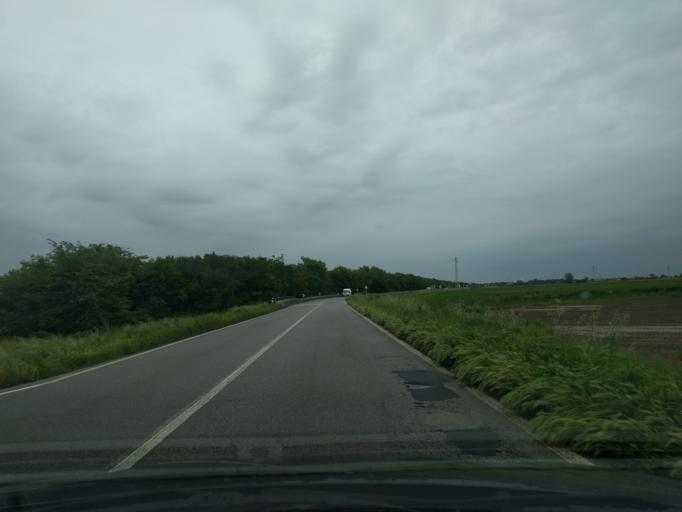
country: IT
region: Veneto
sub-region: Provincia di Rovigo
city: Loreo
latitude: 45.0533
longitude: 12.1580
